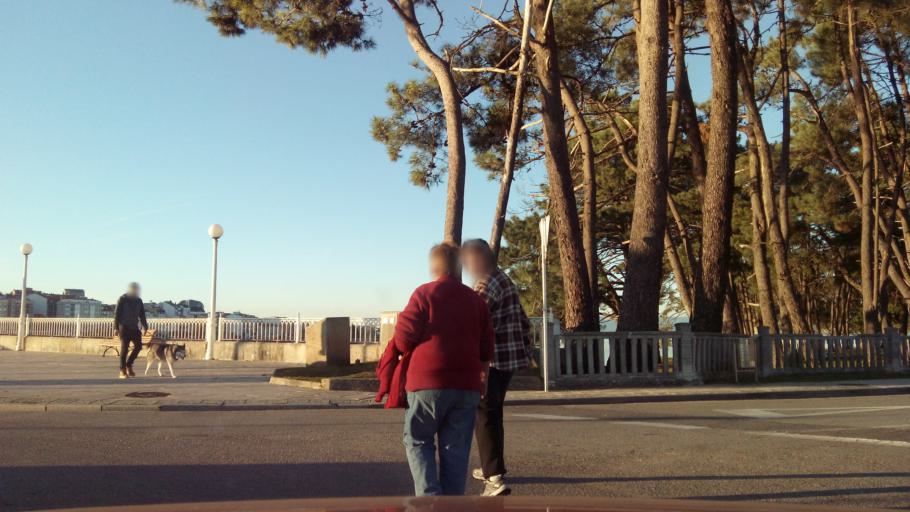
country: ES
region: Galicia
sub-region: Provincia de Pontevedra
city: O Grove
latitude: 42.4875
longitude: -8.8527
